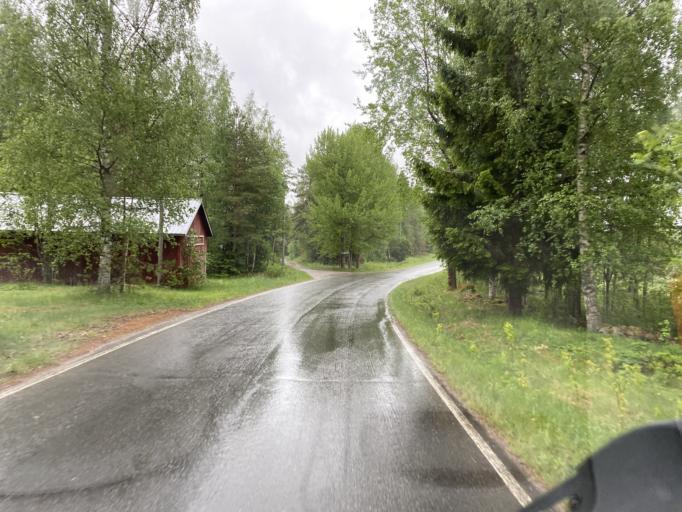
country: FI
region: Haeme
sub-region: Forssa
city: Humppila
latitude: 61.0669
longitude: 23.3206
